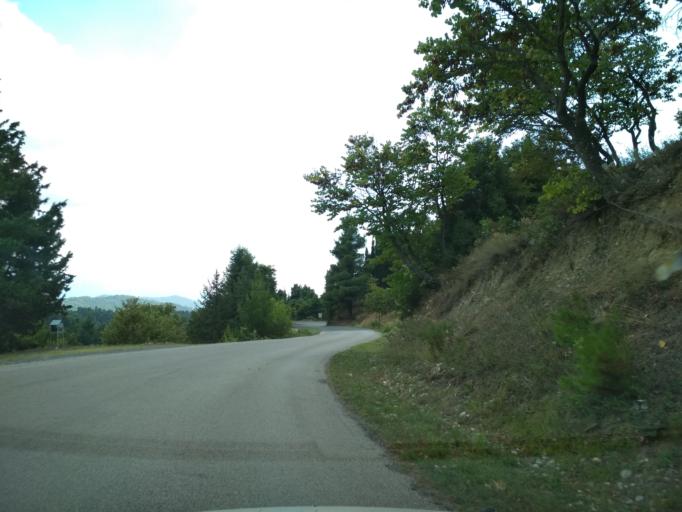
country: GR
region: Central Greece
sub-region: Nomos Evvoias
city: Roviai
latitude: 38.8468
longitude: 23.2828
